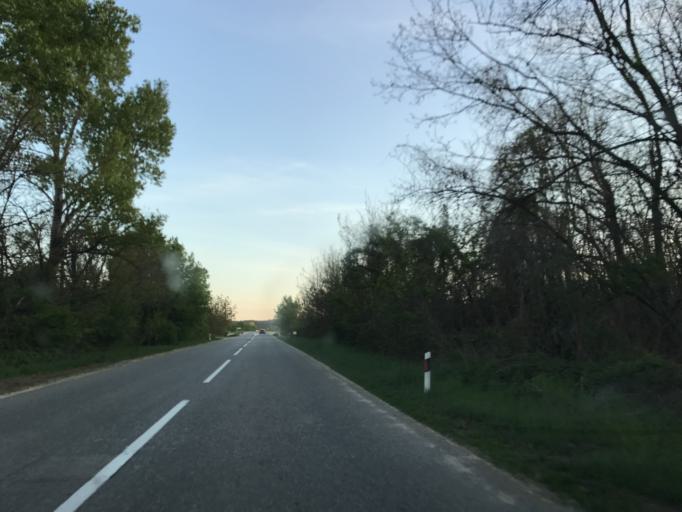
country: RO
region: Mehedinti
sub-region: Comuna Gogosu
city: Ostrovu Mare
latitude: 44.3478
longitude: 22.4754
